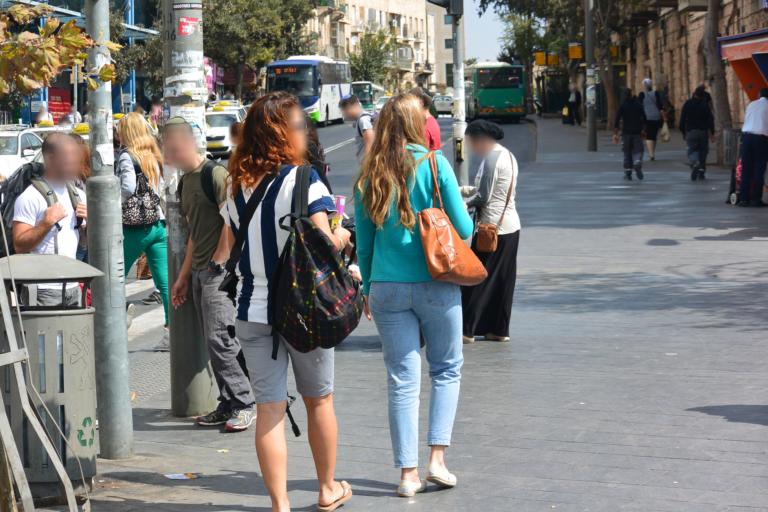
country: IL
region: Jerusalem
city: West Jerusalem
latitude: 31.7886
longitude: 35.2032
